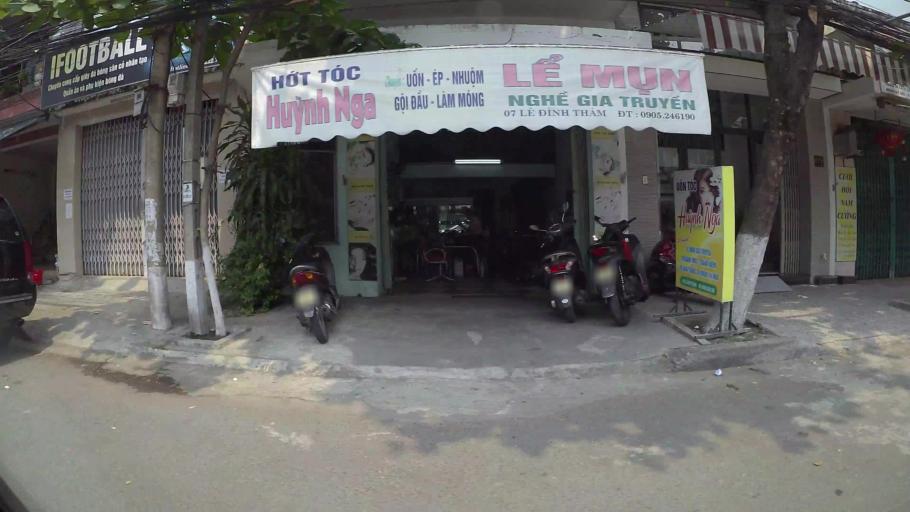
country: VN
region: Da Nang
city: Da Nang
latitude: 16.0505
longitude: 108.2163
